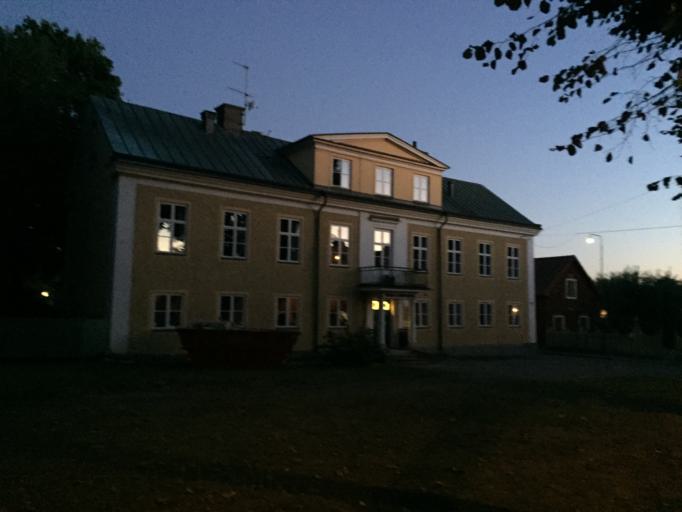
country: SE
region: OEstergoetland
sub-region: Vadstena Kommun
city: Vadstena
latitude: 58.4487
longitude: 14.8933
